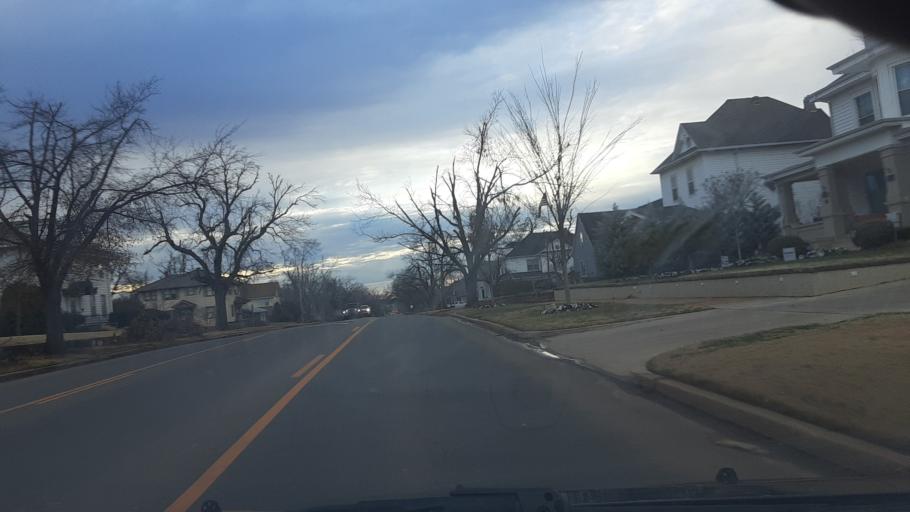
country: US
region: Oklahoma
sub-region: Logan County
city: Guthrie
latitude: 35.8802
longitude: -97.4167
